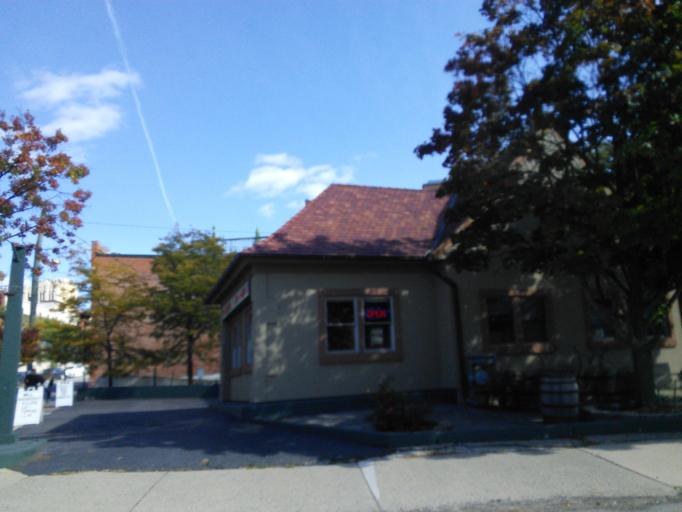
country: US
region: Michigan
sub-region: Washtenaw County
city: Ann Arbor
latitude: 42.2795
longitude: -83.7510
